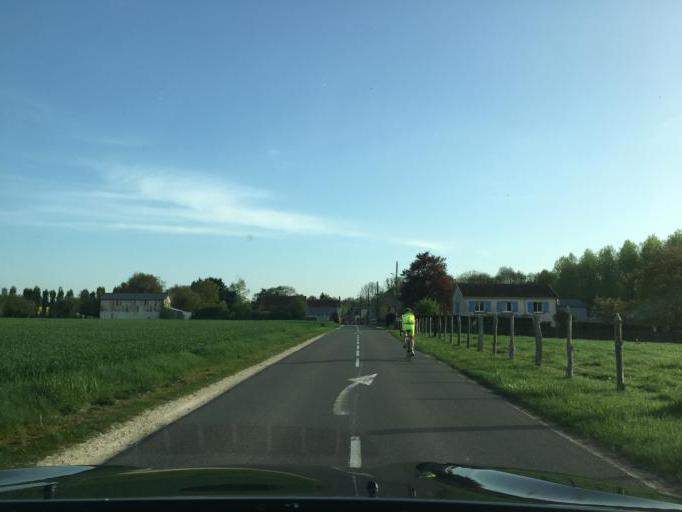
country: FR
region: Centre
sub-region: Departement d'Eure-et-Loir
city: Epernon
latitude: 48.6301
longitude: 1.6792
